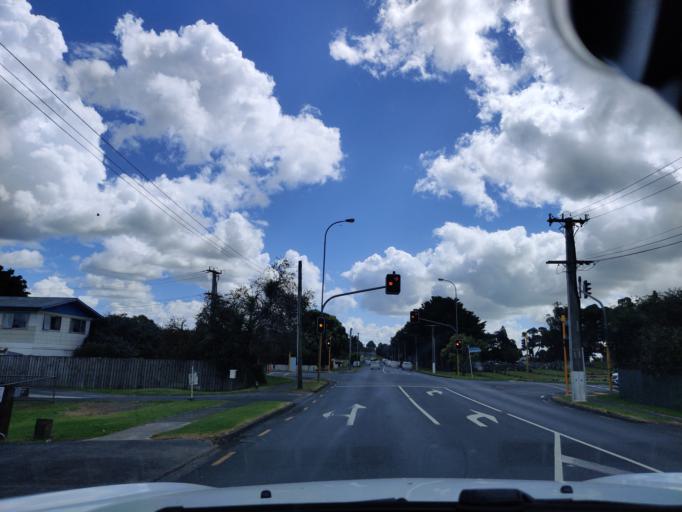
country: NZ
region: Auckland
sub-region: Auckland
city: Papakura
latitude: -37.0696
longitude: 174.9468
